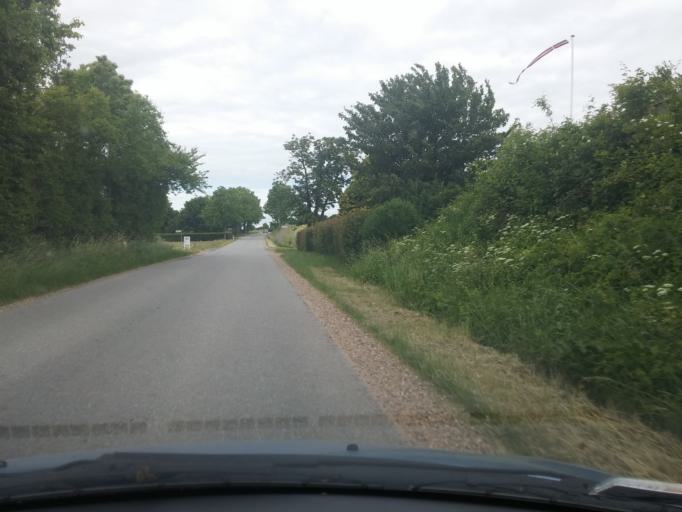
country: DK
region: South Denmark
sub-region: Aabenraa Kommune
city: Lojt Kirkeby
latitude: 55.1529
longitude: 9.4721
